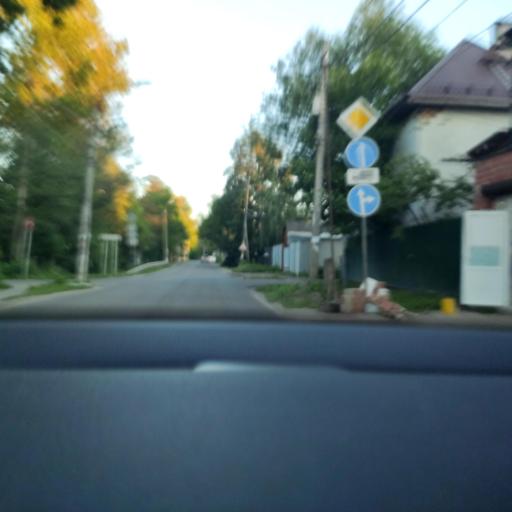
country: RU
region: Moskovskaya
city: Reutov
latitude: 55.7642
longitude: 37.8961
